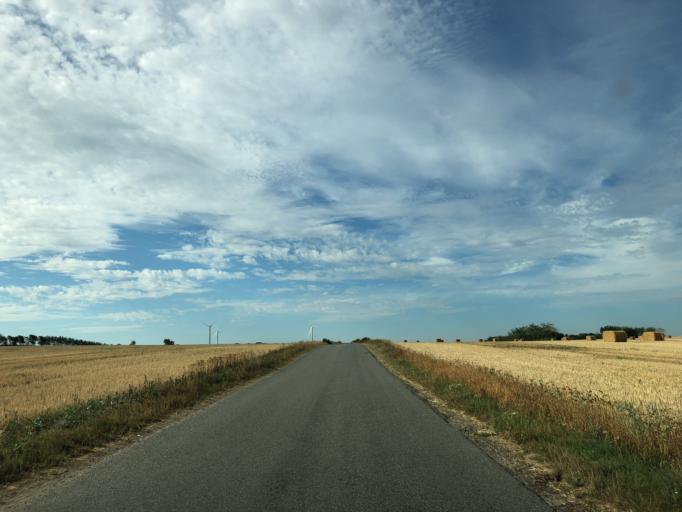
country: DK
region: Central Jutland
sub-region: Ringkobing-Skjern Kommune
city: Skjern
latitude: 56.0690
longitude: 8.4158
